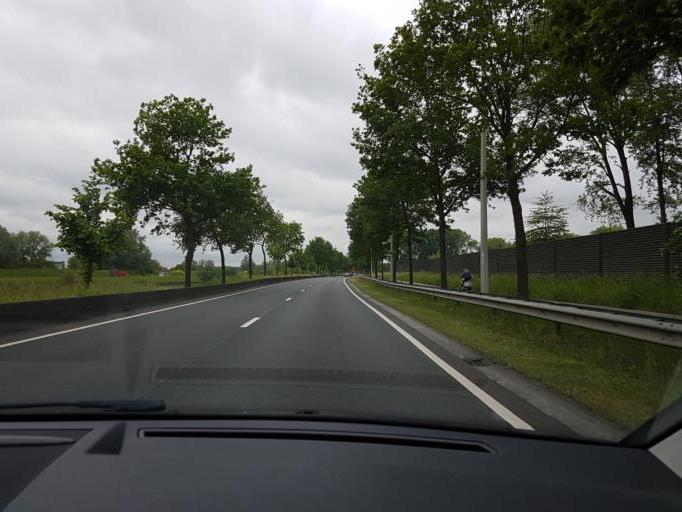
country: BE
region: Flanders
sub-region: Provincie Oost-Vlaanderen
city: Sint-Martens-Latem
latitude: 51.0615
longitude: 3.6622
